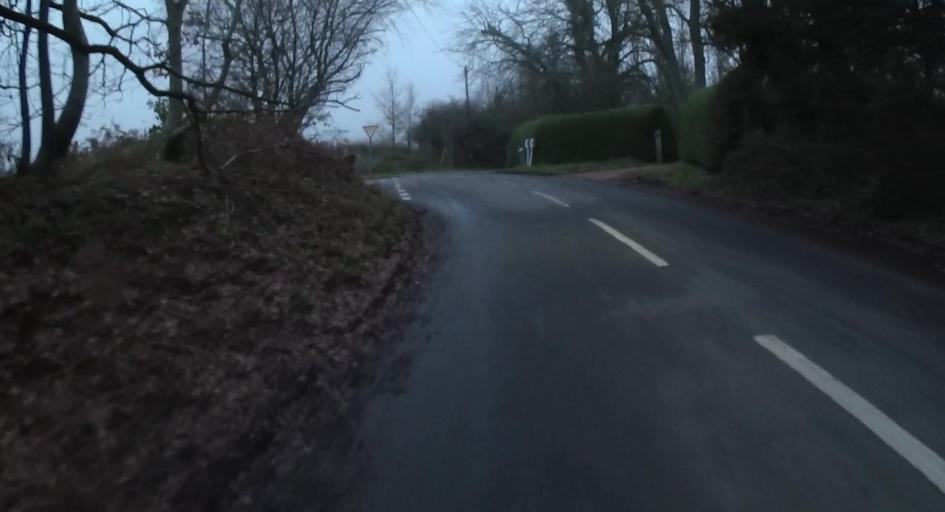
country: GB
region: England
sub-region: Hampshire
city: Tadley
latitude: 51.3450
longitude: -1.0859
